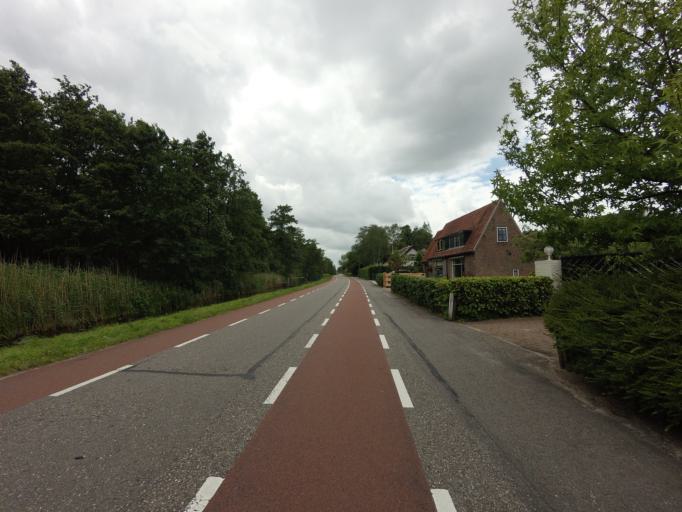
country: NL
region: North Holland
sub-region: Gemeente Wijdemeren
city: Oud-Loosdrecht
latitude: 52.2231
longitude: 5.0788
